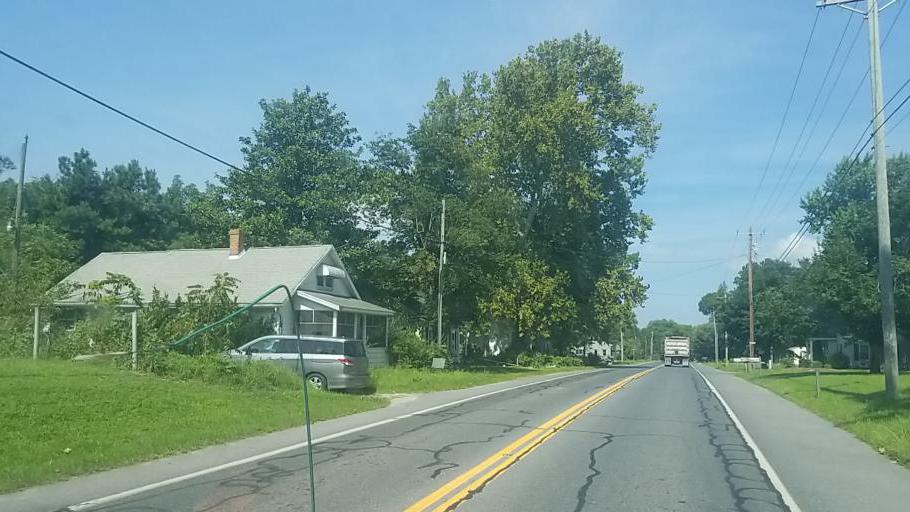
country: US
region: Delaware
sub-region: Sussex County
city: Seaford
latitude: 38.6668
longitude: -75.5677
